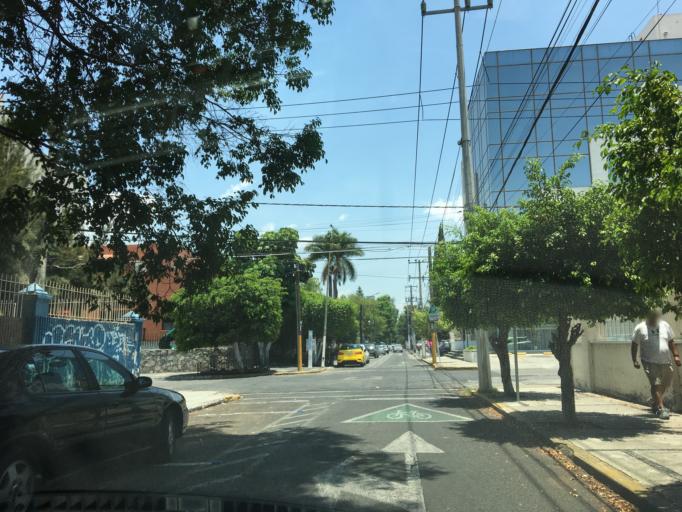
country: MX
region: Jalisco
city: Guadalajara
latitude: 20.6757
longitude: -103.3717
